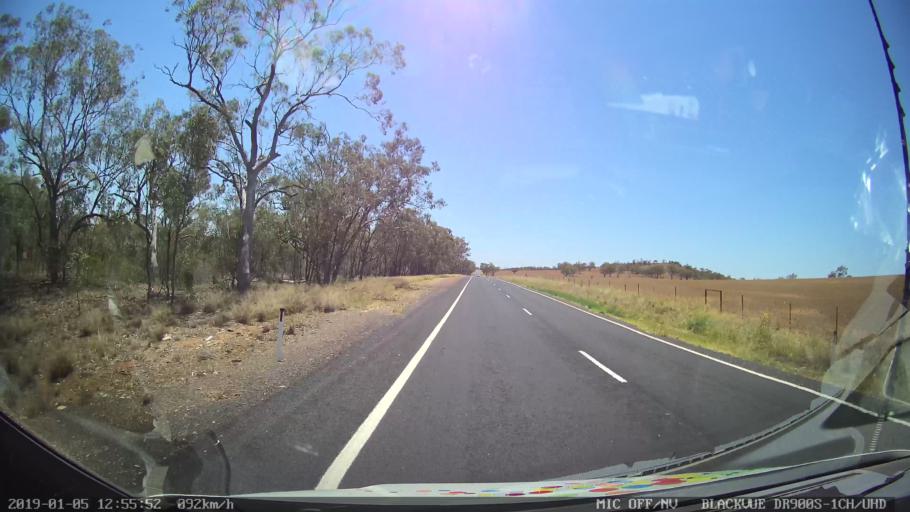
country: AU
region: New South Wales
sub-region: Warrumbungle Shire
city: Coonabarabran
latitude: -31.1186
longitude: 149.7123
